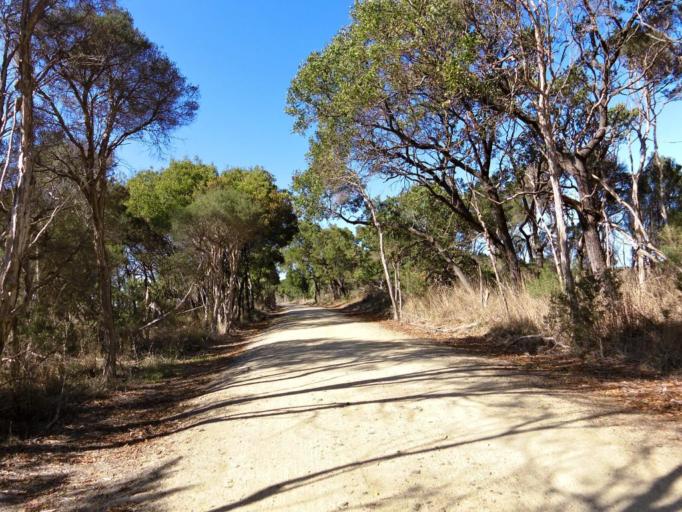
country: AU
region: Victoria
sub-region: Bass Coast
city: North Wonthaggi
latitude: -38.5894
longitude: 145.5584
